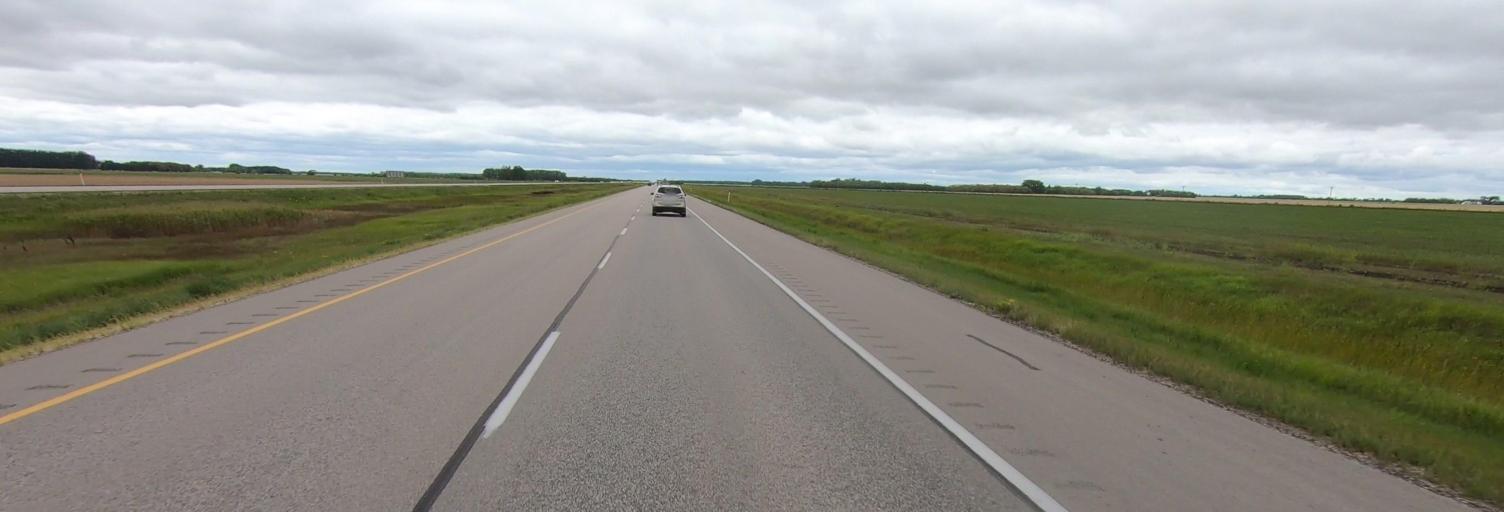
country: CA
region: Manitoba
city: Portage la Prairie
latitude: 49.9420
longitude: -97.9462
